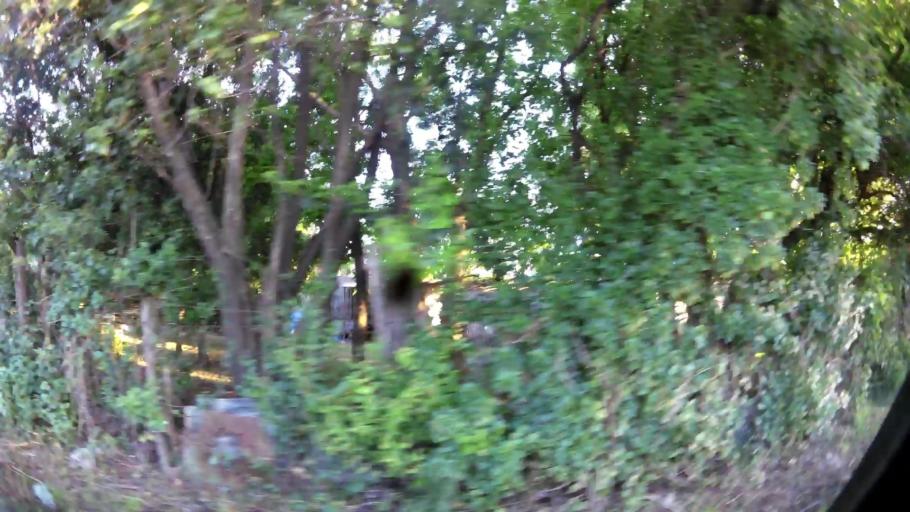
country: AR
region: Buenos Aires
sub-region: Partido de Almirante Brown
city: Adrogue
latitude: -34.7871
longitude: -58.3391
